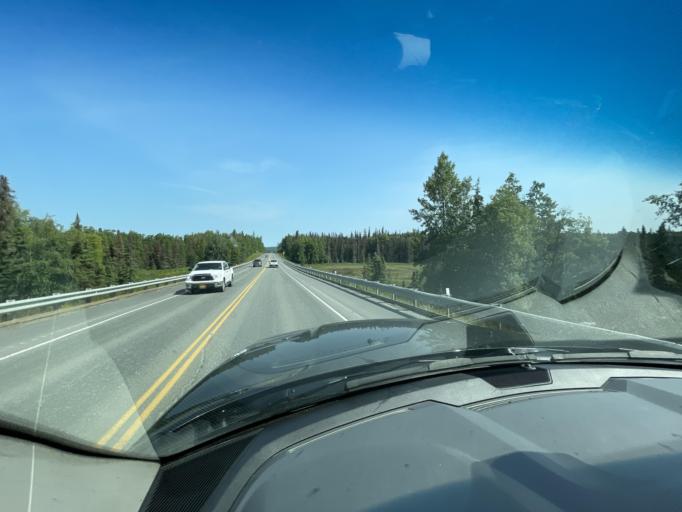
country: US
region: Alaska
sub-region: Kenai Peninsula Borough
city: Soldotna
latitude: 60.4615
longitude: -151.0946
